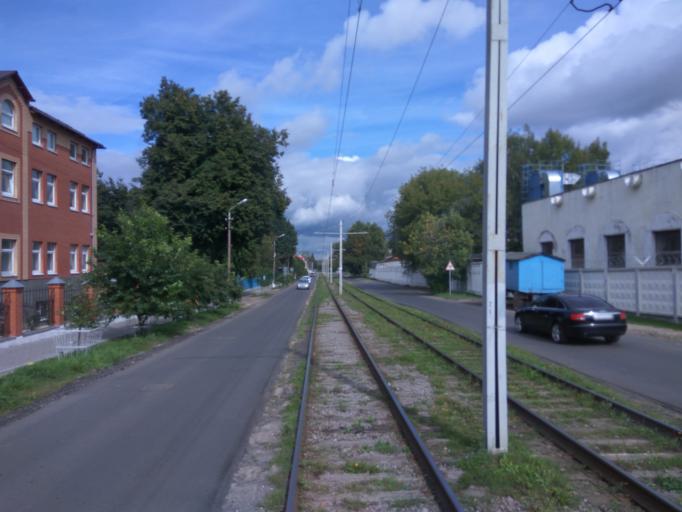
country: RU
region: Moskovskaya
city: Kolomna
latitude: 55.0963
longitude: 38.7716
